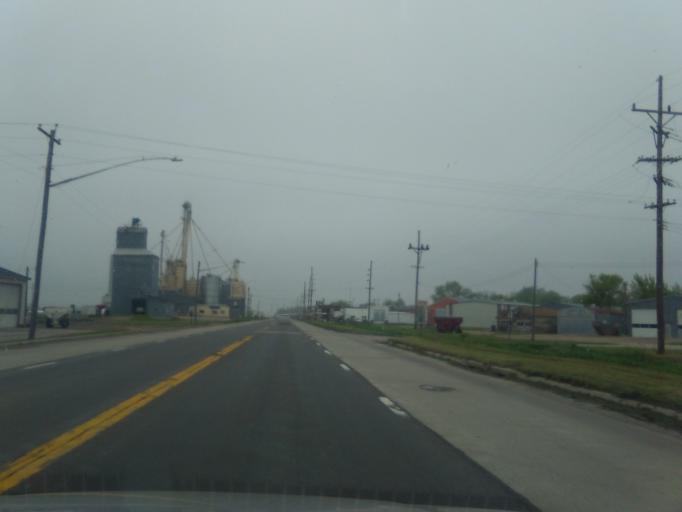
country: US
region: Nebraska
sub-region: Cuming County
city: Wisner
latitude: 41.9268
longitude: -96.8088
